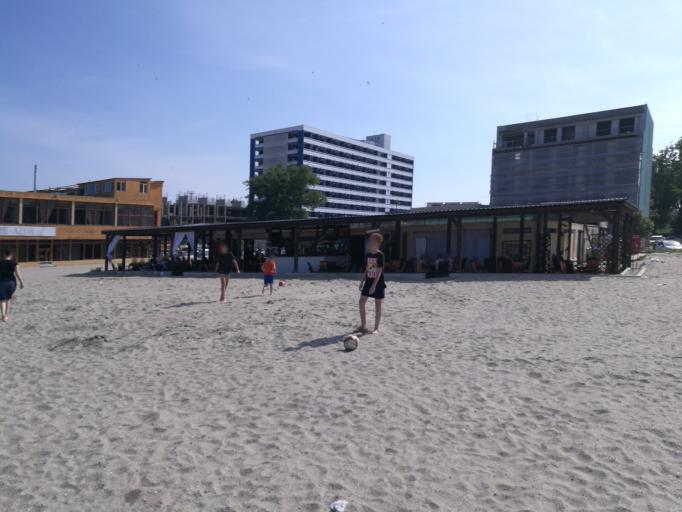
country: RO
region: Constanta
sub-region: Municipiul Constanta
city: Palazu Mare
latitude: 44.2245
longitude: 28.6326
